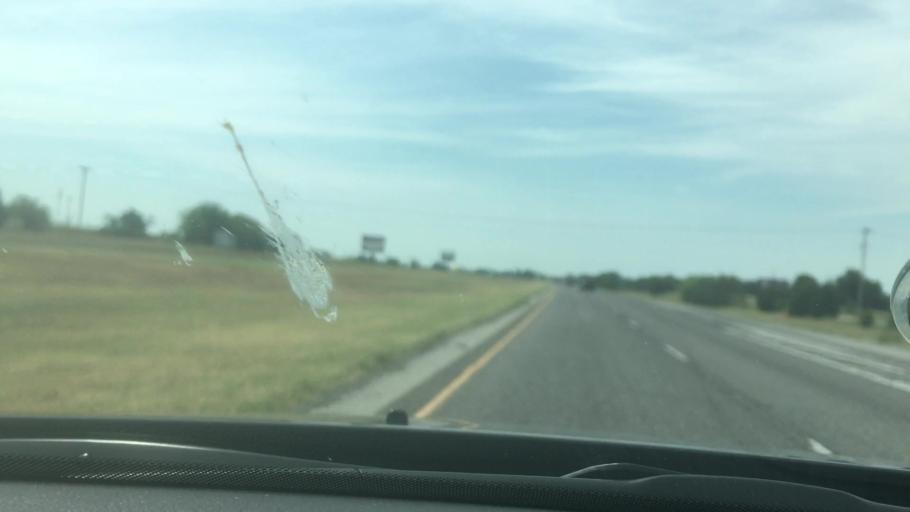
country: US
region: Oklahoma
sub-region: Garvin County
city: Wynnewood
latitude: 34.5681
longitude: -97.1976
